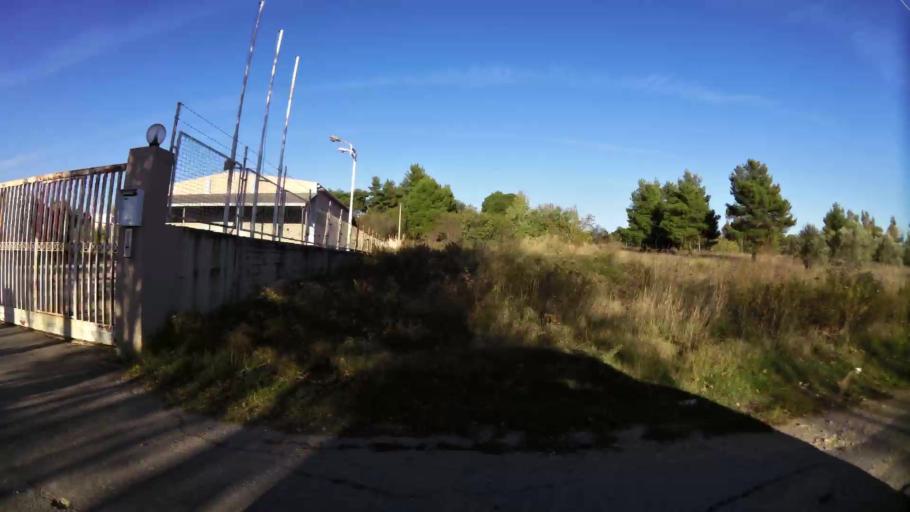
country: GR
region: Attica
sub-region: Nomarchia Anatolikis Attikis
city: Anoixi
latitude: 38.1336
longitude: 23.8525
